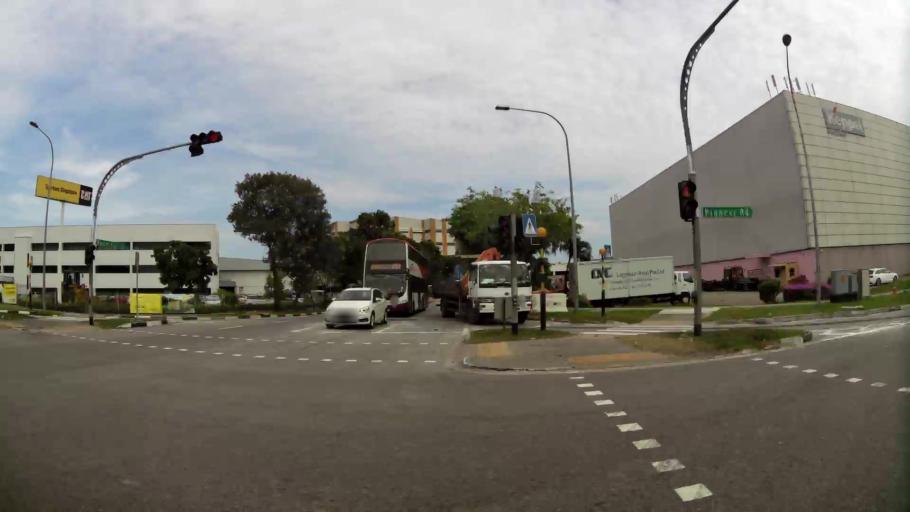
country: SG
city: Singapore
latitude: 1.3152
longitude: 103.6909
